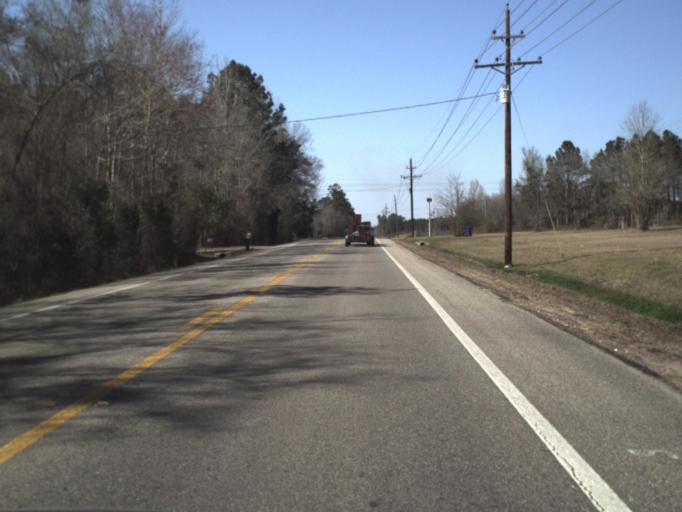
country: US
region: Florida
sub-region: Calhoun County
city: Blountstown
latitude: 30.5116
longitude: -85.1220
